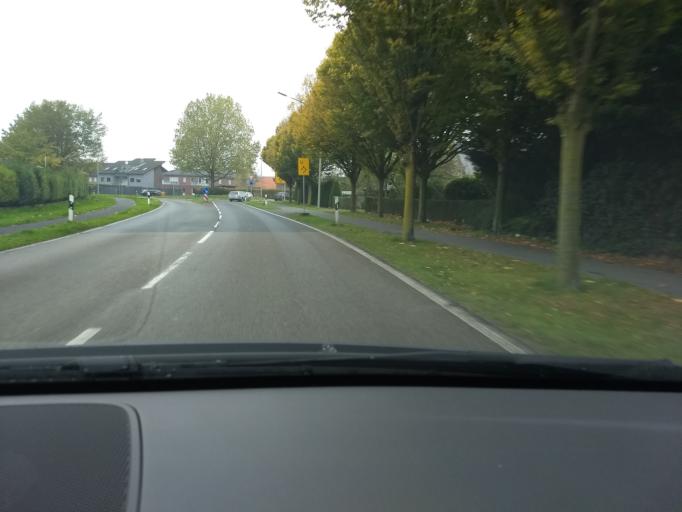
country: DE
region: North Rhine-Westphalia
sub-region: Regierungsbezirk Munster
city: Sudlohn
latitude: 51.9480
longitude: 6.8632
